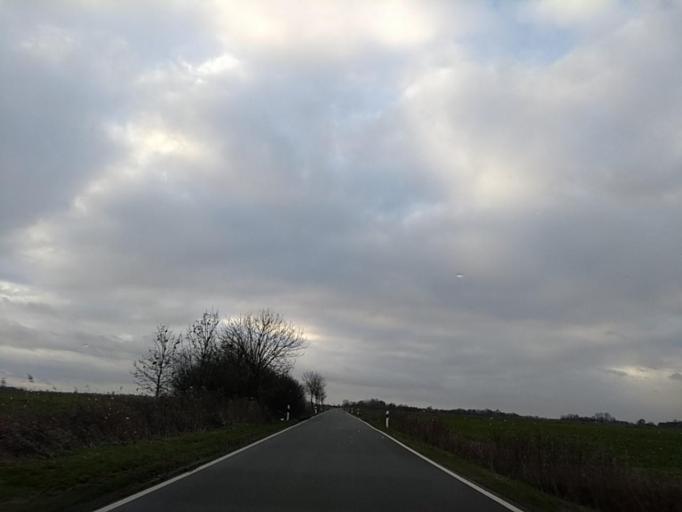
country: DE
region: Lower Saxony
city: Emden
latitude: 53.2956
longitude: 7.2779
